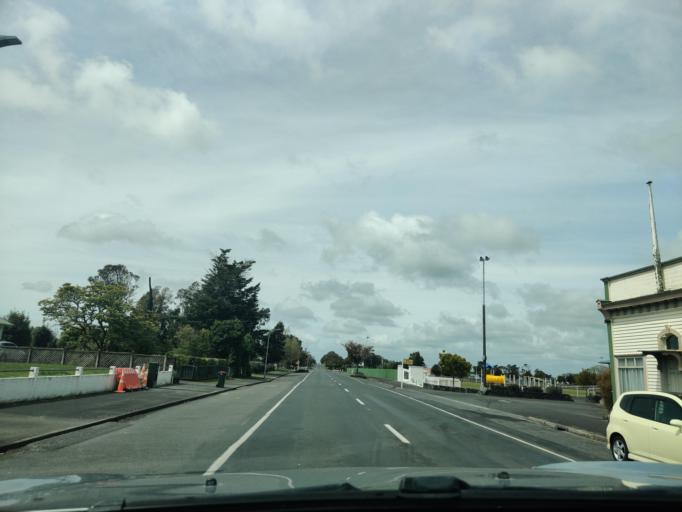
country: NZ
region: Taranaki
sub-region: South Taranaki District
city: Eltham
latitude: -39.4291
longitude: 174.1506
